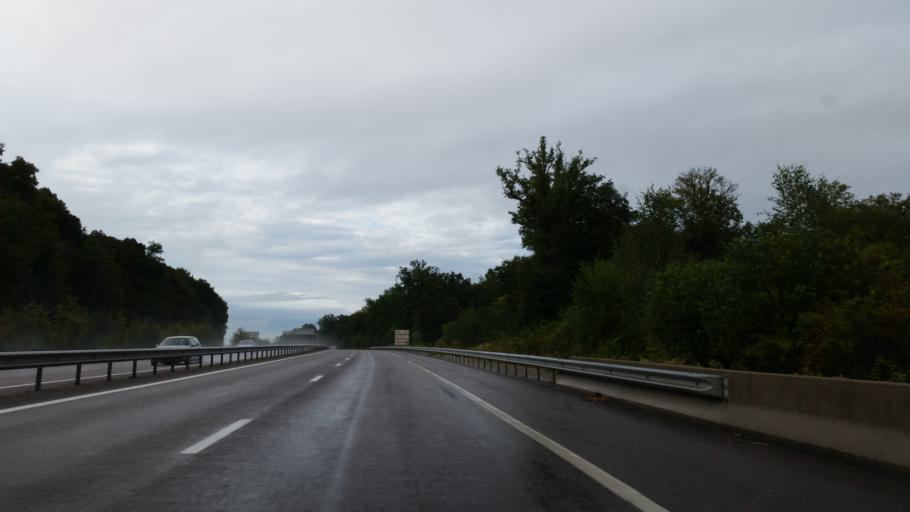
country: FR
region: Franche-Comte
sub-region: Departement de la Haute-Saone
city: Lure
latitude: 47.6864
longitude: 6.5152
